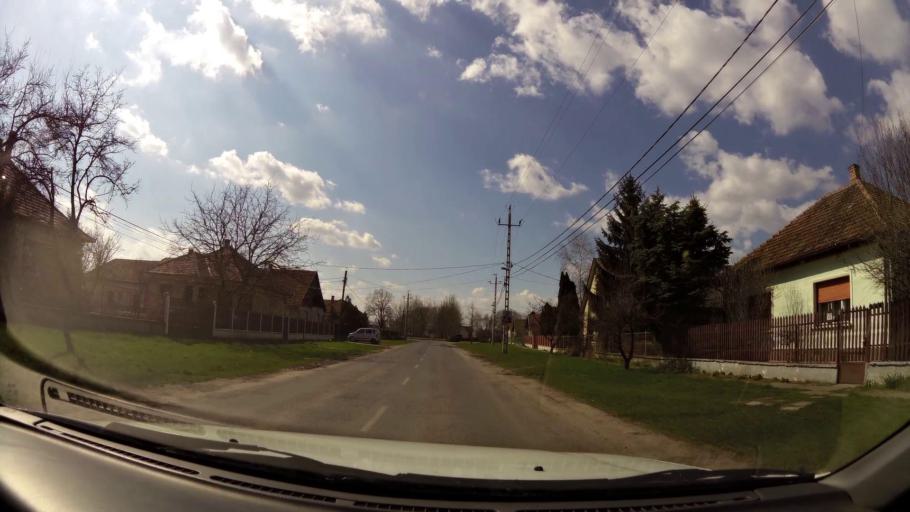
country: HU
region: Pest
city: Tapiogyorgye
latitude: 47.3402
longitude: 19.9415
